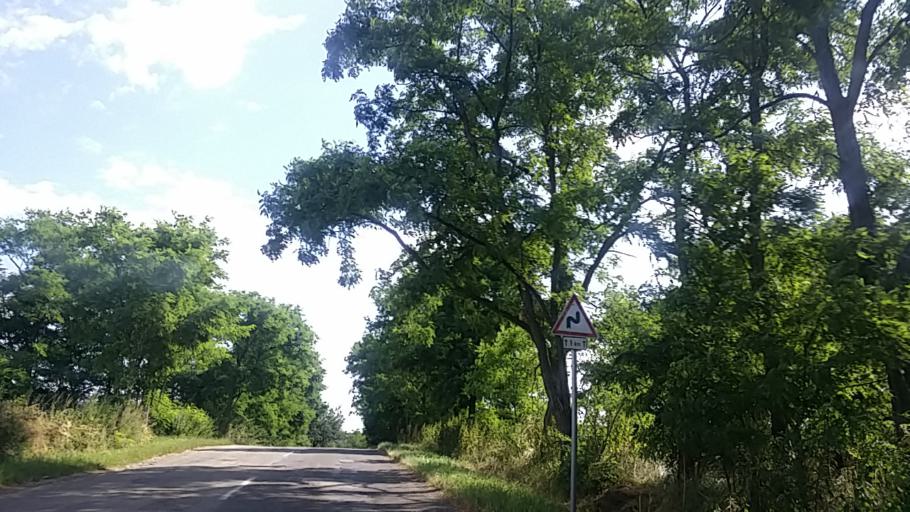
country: HU
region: Nograd
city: Romhany
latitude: 47.8477
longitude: 19.2565
